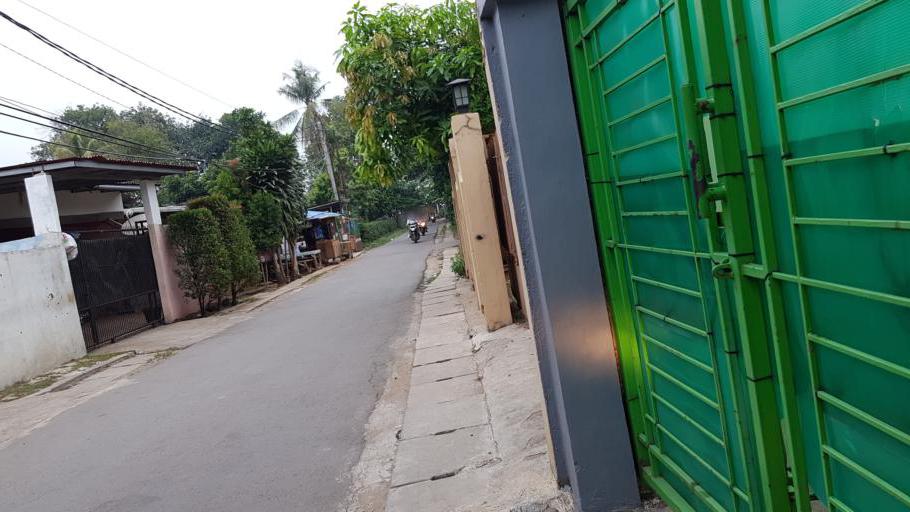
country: ID
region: West Java
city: Sawangan
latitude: -6.3988
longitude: 106.7659
